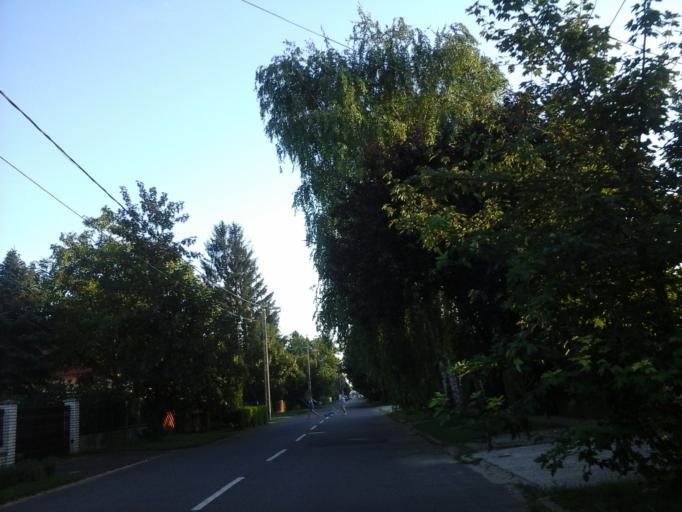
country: HU
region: Hajdu-Bihar
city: Hajduszoboszlo
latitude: 47.4587
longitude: 21.4058
